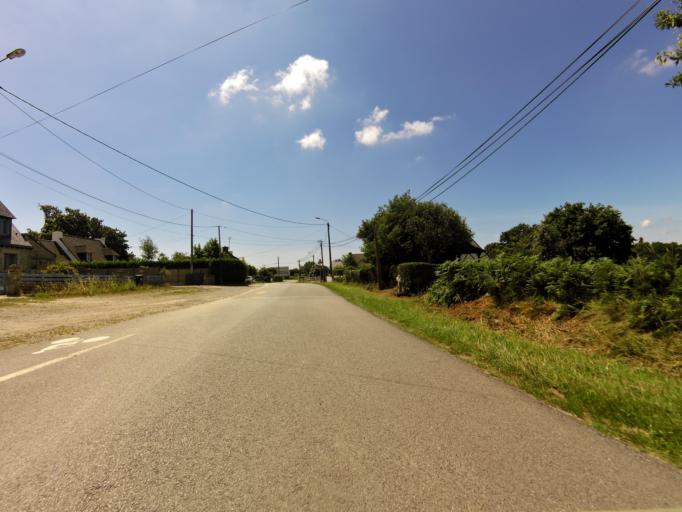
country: FR
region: Brittany
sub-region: Departement du Morbihan
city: Theix
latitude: 47.6061
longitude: -2.6788
